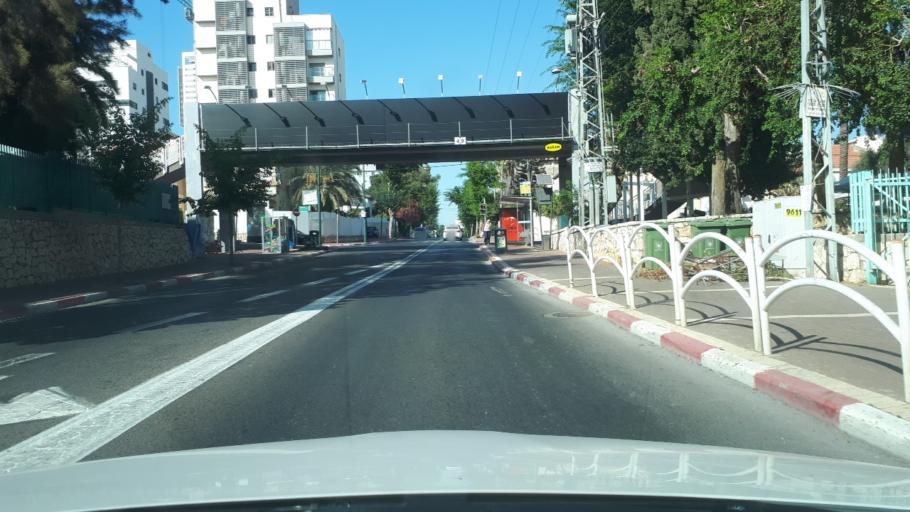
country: IL
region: Tel Aviv
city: Giv`atayim
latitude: 32.0662
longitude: 34.8240
